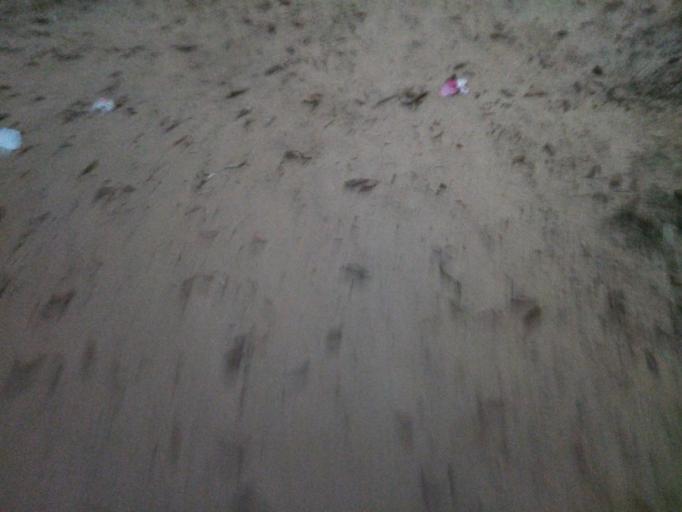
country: BD
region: Chittagong
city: Cox's Bazar
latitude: 21.6280
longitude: 92.0774
